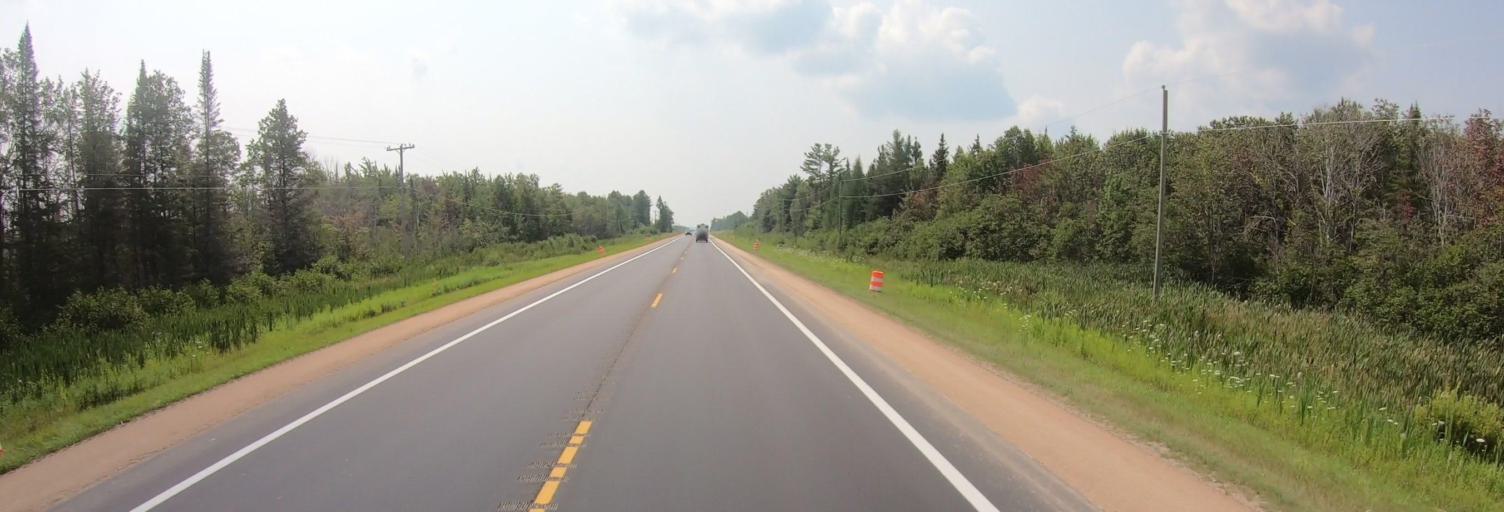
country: US
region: Michigan
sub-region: Luce County
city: Newberry
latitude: 46.4078
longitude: -85.5100
